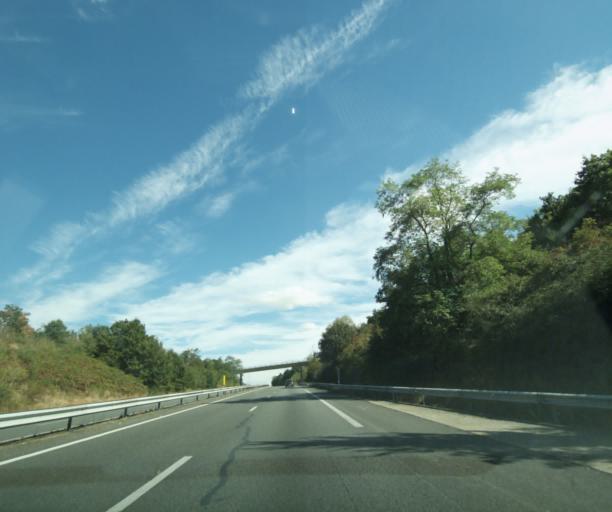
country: FR
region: Midi-Pyrenees
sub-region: Departement du Tarn-et-Garonne
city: Lamagistere
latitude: 44.0703
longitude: 0.8184
